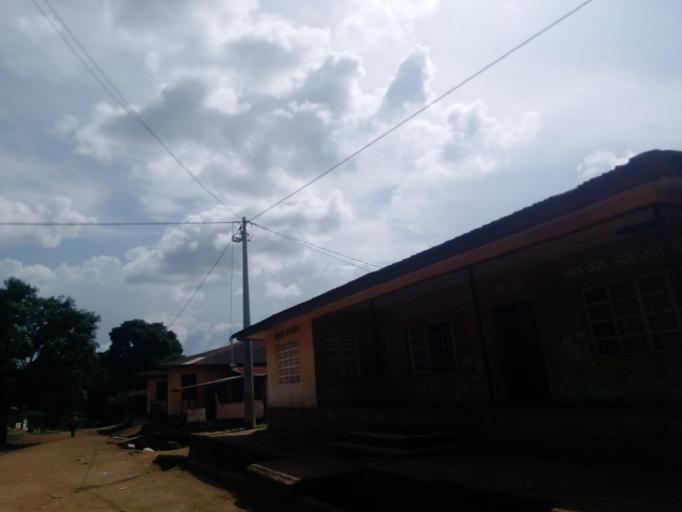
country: SL
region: Northern Province
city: Makeni
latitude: 8.8974
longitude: -12.0437
